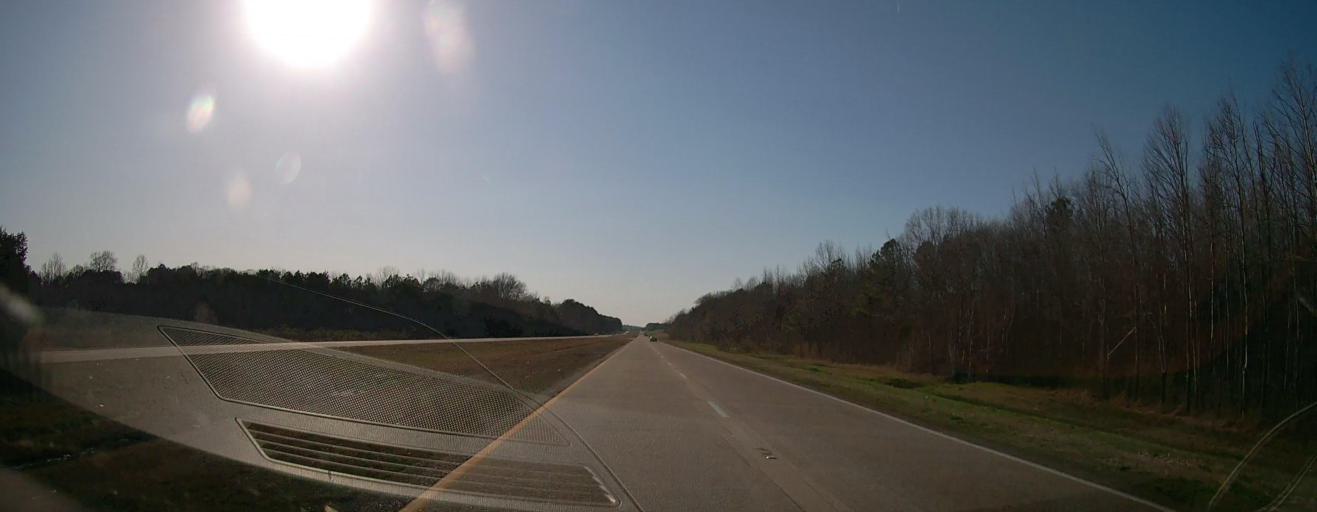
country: US
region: Mississippi
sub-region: Tishomingo County
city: Iuka
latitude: 34.8048
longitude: -88.2462
